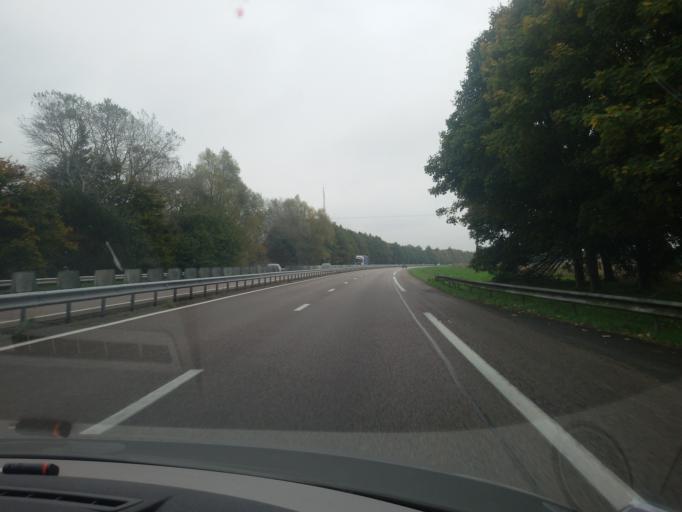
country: FR
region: Haute-Normandie
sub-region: Departement de l'Eure
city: Manneville-sur-Risle
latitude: 49.3947
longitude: 0.5376
